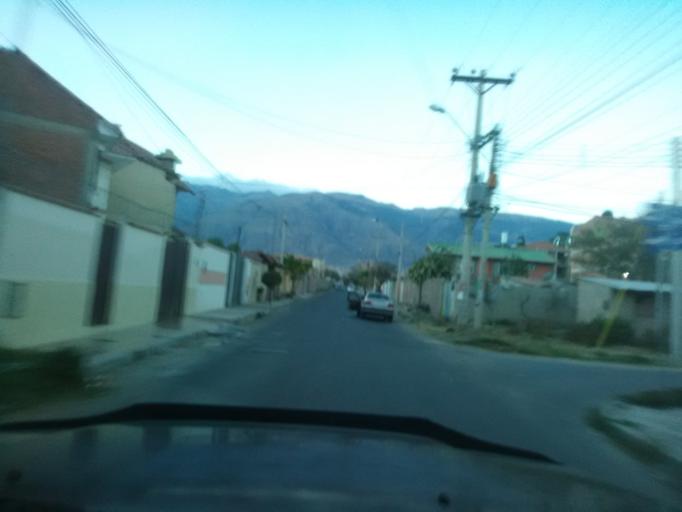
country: BO
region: Cochabamba
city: Cochabamba
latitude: -17.3729
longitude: -66.1908
